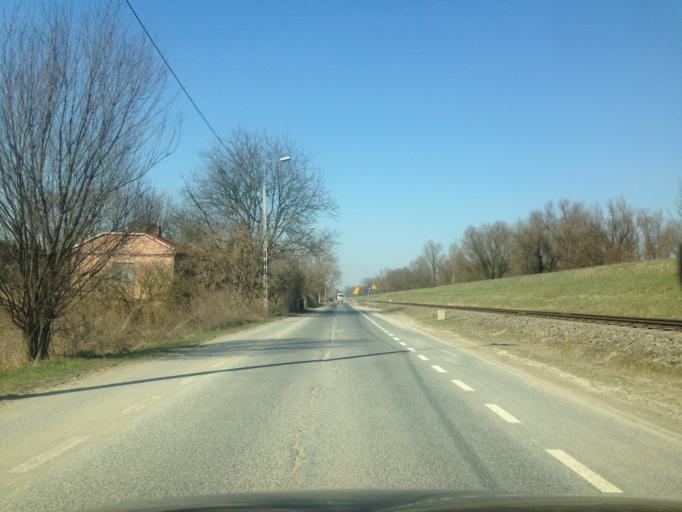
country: PL
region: Masovian Voivodeship
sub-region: Warszawa
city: Wilanow
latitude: 52.1753
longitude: 21.1179
